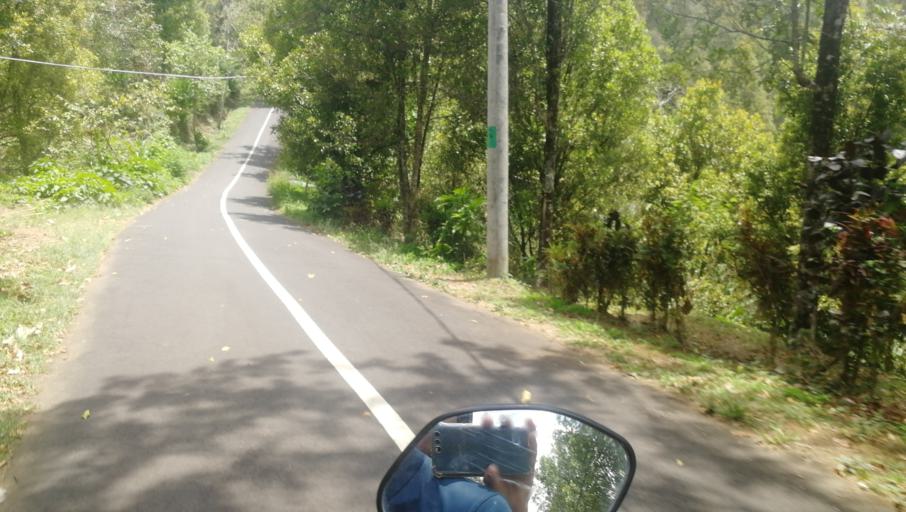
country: ID
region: Bali
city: Munduk
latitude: -8.2963
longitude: 115.0494
